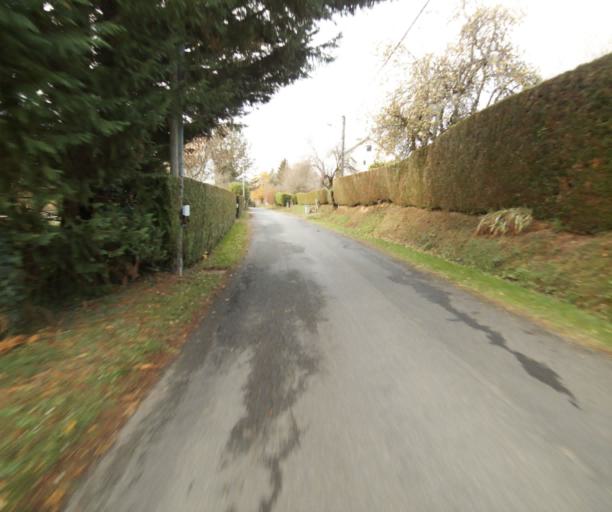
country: FR
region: Limousin
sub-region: Departement de la Correze
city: Laguenne
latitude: 45.2335
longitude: 1.7888
